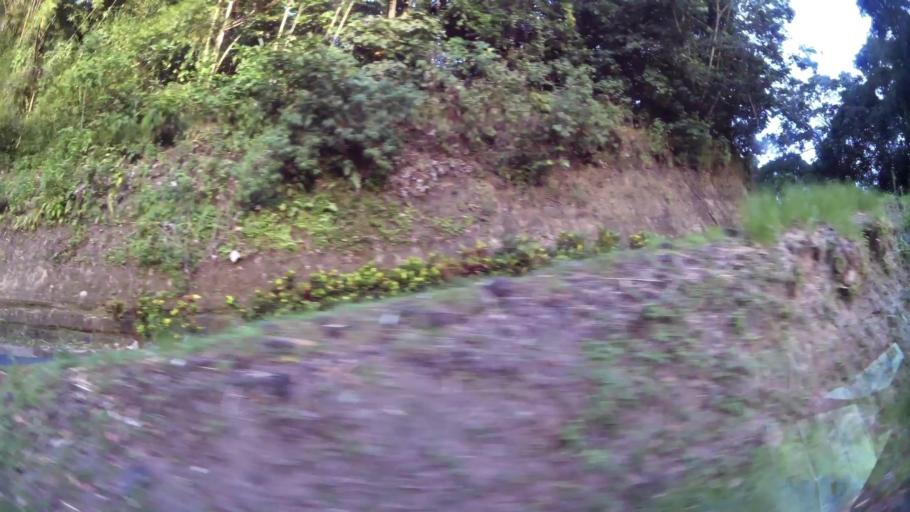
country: DM
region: Saint Andrew
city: Calibishie
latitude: 15.5859
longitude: -61.4059
